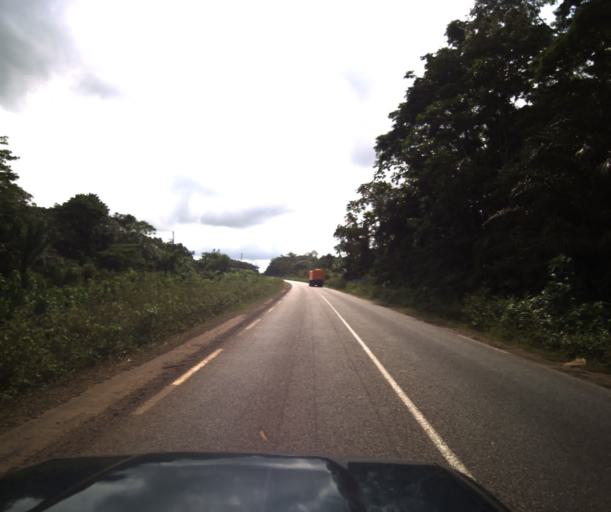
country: CM
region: Littoral
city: Edea
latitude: 3.8064
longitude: 10.2623
